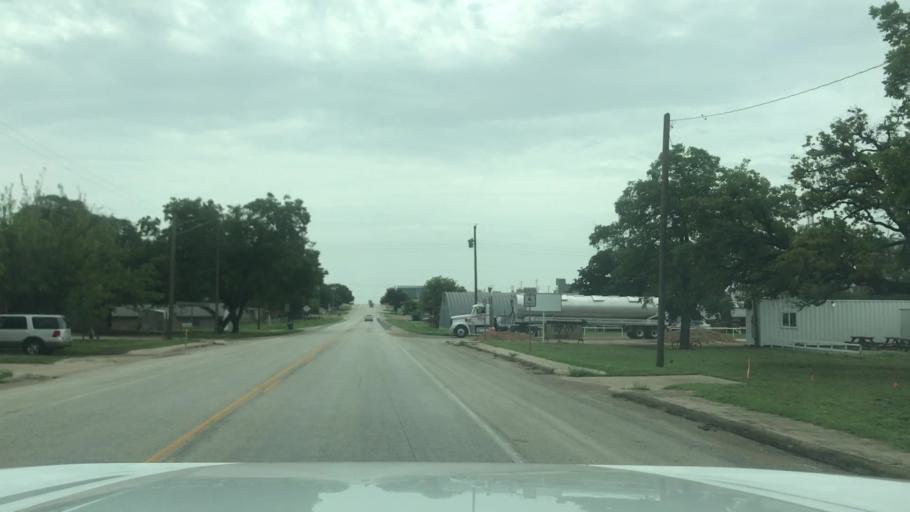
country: US
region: Texas
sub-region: Eastland County
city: Gorman
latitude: 32.2134
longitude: -98.6704
